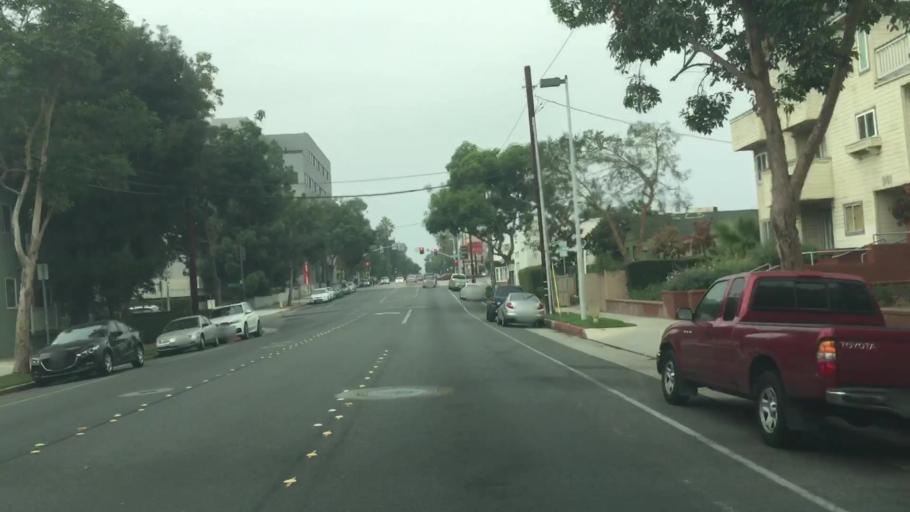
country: US
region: California
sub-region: Los Angeles County
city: Pasadena
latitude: 34.1359
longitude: -118.1303
